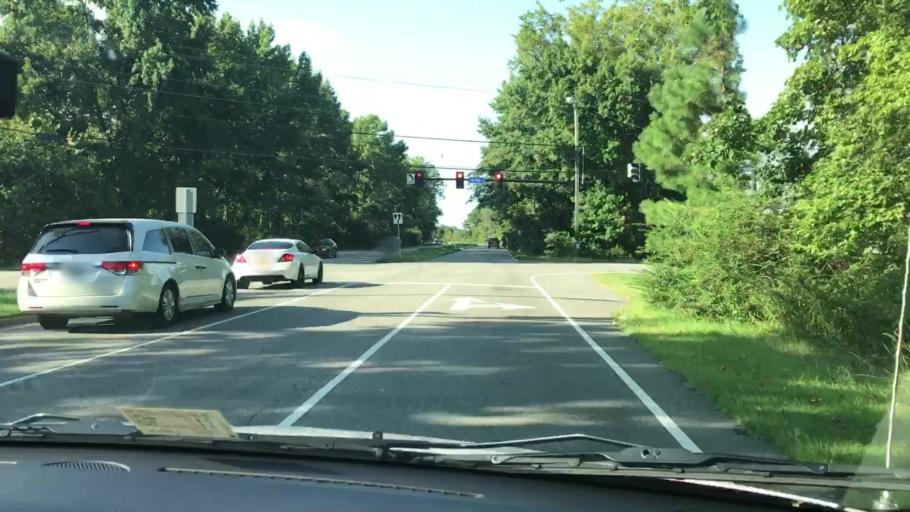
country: US
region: Virginia
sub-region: City of Hampton
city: Hampton
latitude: 37.0593
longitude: -76.3658
